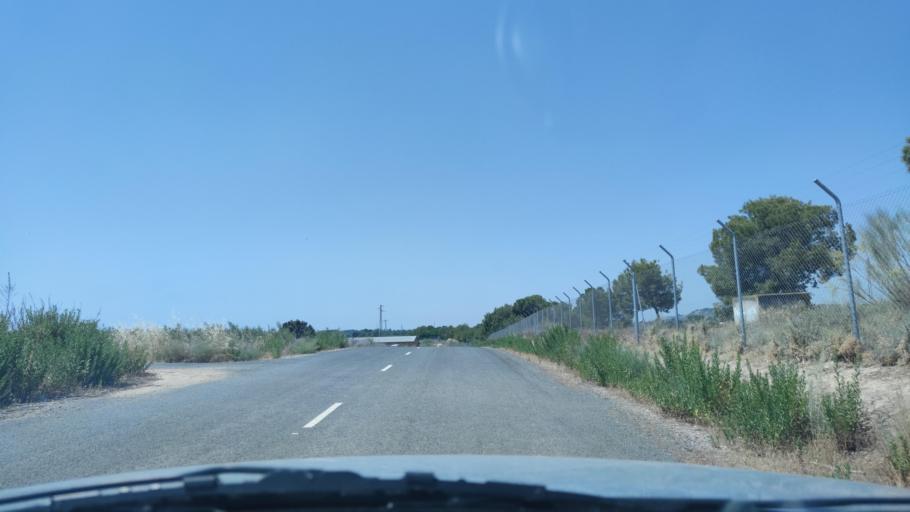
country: ES
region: Catalonia
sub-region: Provincia de Lleida
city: Alpicat
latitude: 41.6556
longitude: 0.5796
